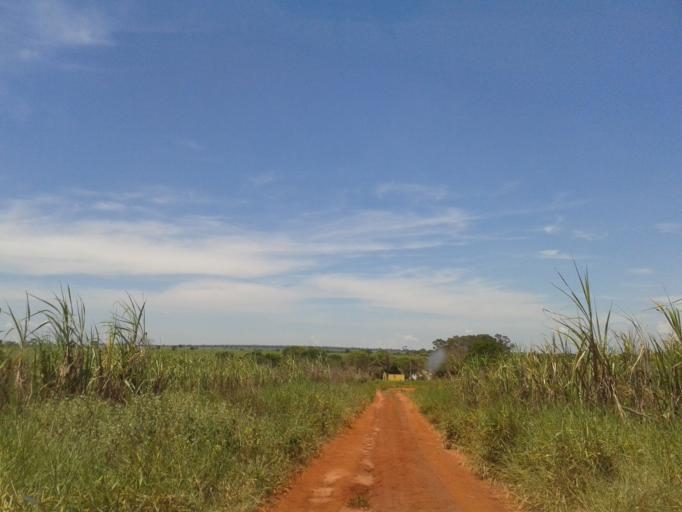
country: BR
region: Minas Gerais
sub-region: Santa Vitoria
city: Santa Vitoria
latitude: -19.1634
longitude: -50.5515
